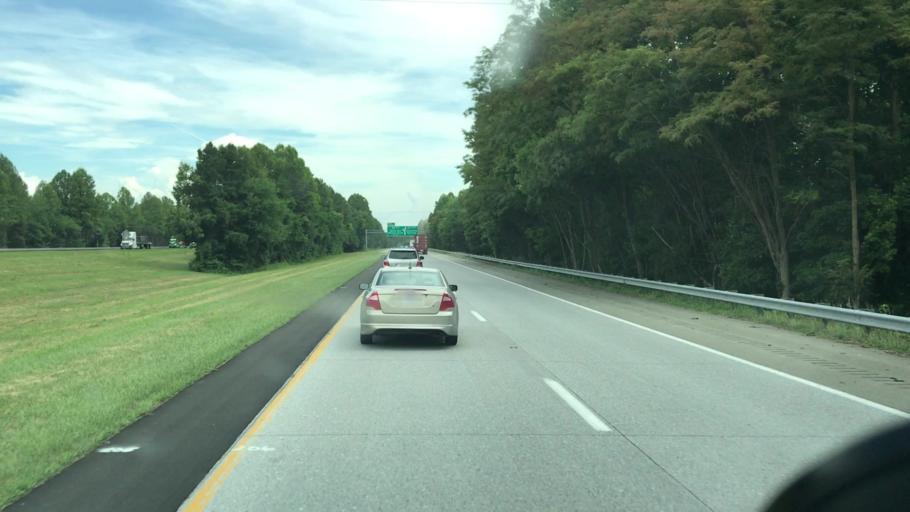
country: US
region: Virginia
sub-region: Carroll County
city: Cana
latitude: 36.5082
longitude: -80.7423
